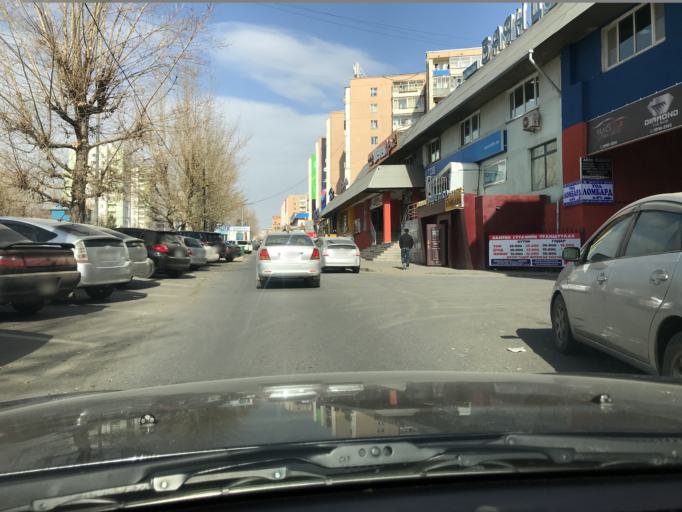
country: MN
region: Ulaanbaatar
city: Ulaanbaatar
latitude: 47.9206
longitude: 106.9432
